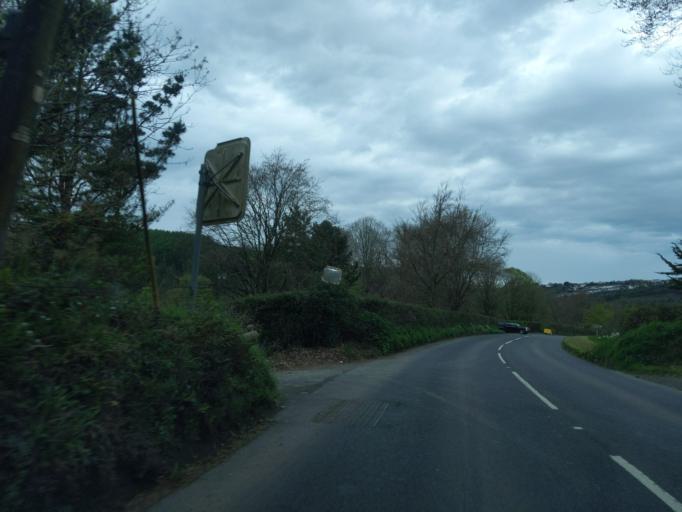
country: GB
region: England
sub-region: Devon
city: Great Torrington
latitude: 50.9376
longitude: -4.1350
